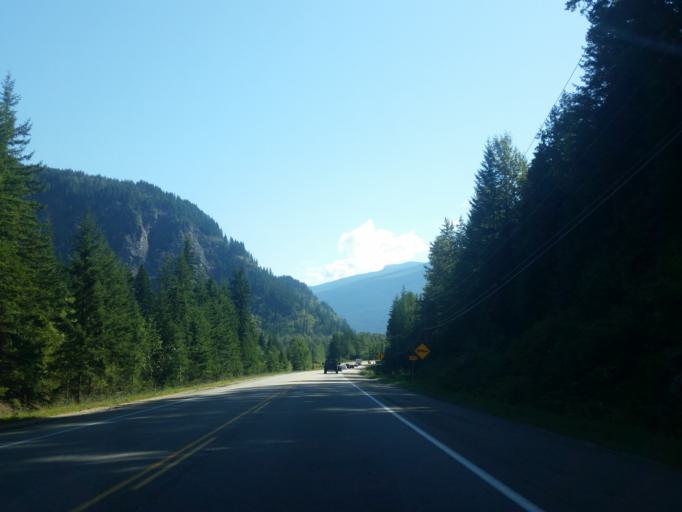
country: CA
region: British Columbia
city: Sicamous
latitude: 50.8907
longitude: -118.8728
